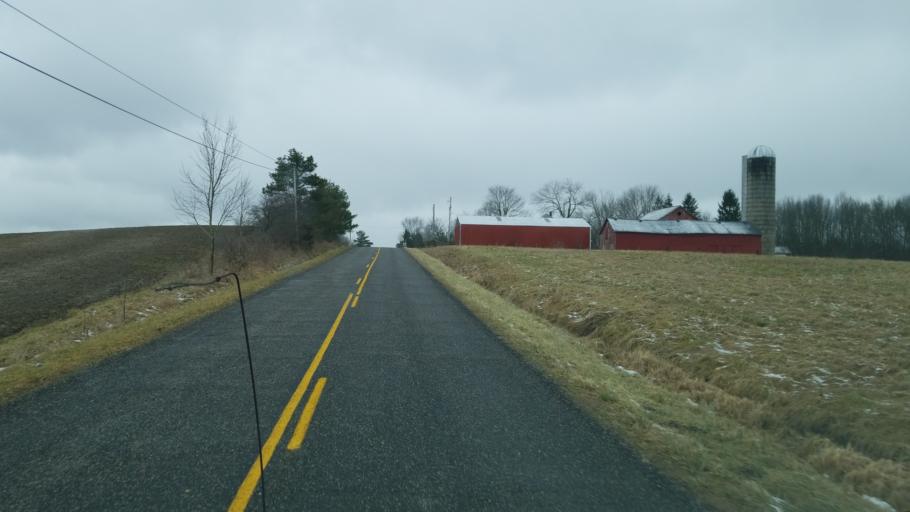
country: US
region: Ohio
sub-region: Portage County
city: Windham
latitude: 41.3319
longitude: -80.9834
